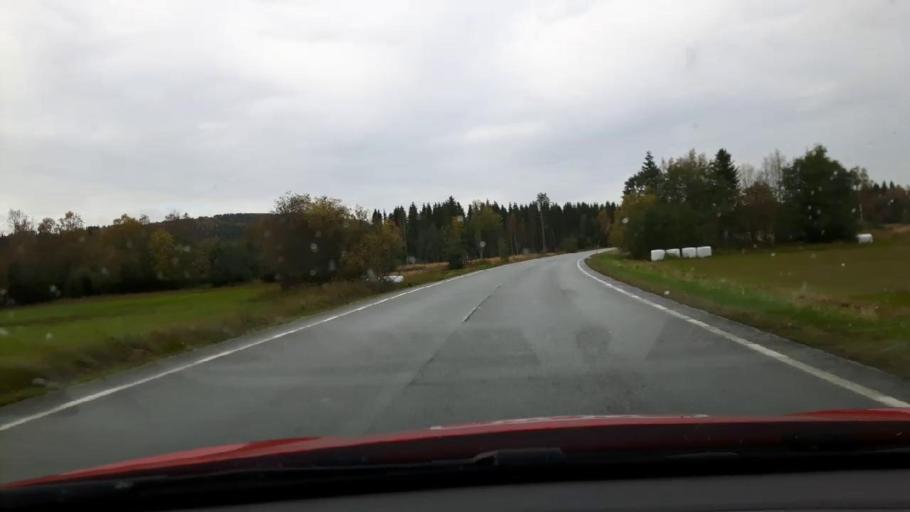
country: SE
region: Jaemtland
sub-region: Bergs Kommun
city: Hoverberg
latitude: 62.9057
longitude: 14.3344
